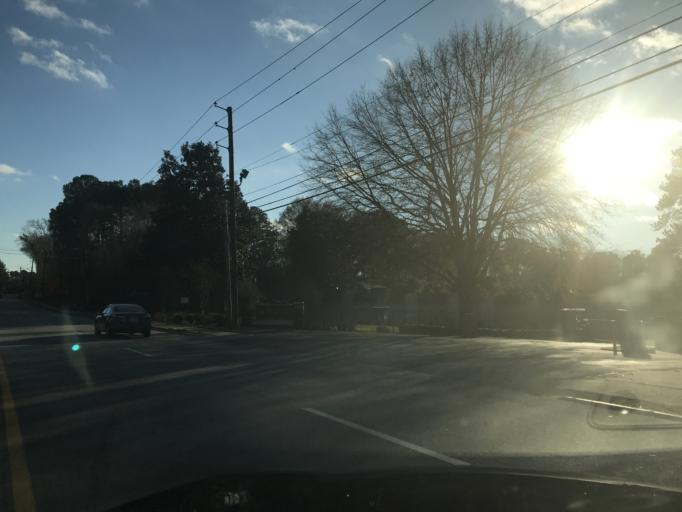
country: US
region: Georgia
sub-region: Fulton County
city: College Park
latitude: 33.6317
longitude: -84.4923
